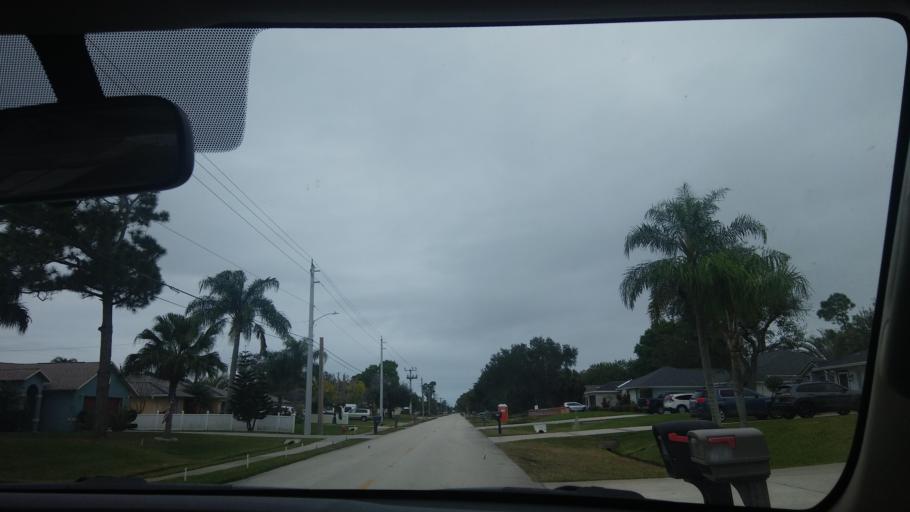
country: US
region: Florida
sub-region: Indian River County
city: Sebastian
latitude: 27.7910
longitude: -80.4948
